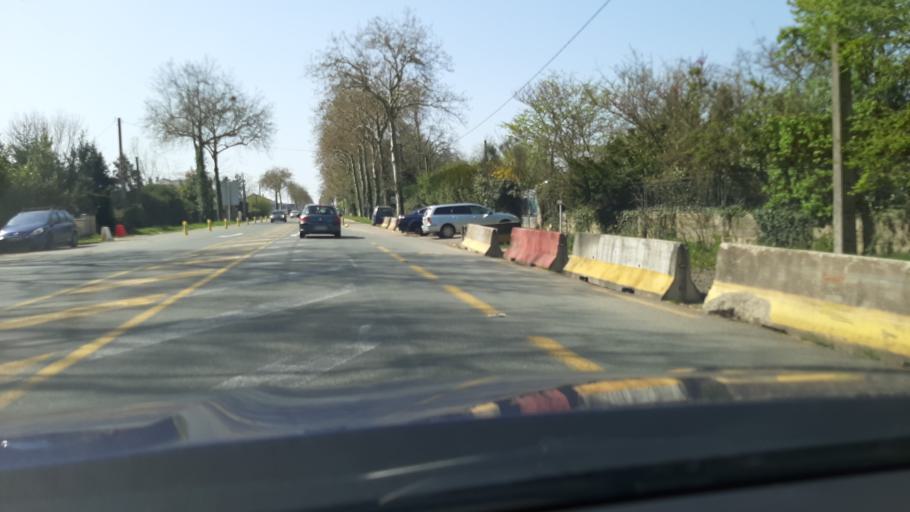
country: FR
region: Pays de la Loire
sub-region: Departement de Maine-et-Loire
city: Ecouflant
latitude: 47.4915
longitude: -0.5042
